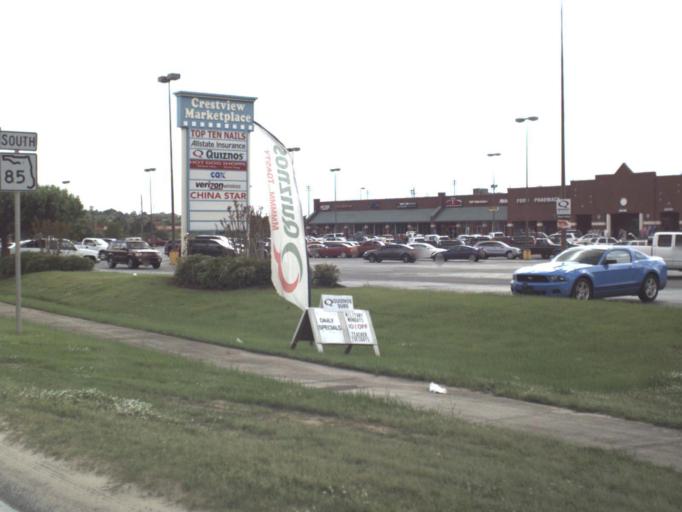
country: US
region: Florida
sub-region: Okaloosa County
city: Crestview
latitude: 30.7942
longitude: -86.5576
